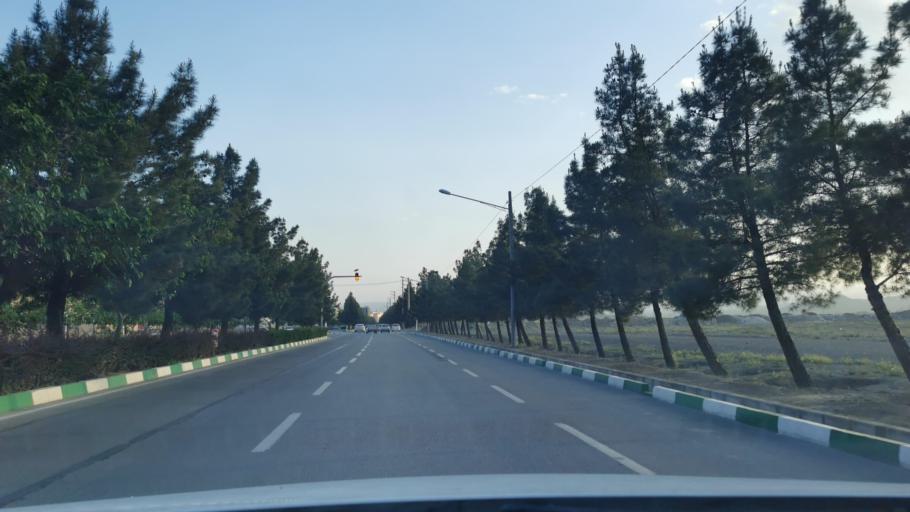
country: IR
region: Razavi Khorasan
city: Torqabeh
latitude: 36.3873
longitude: 59.4664
